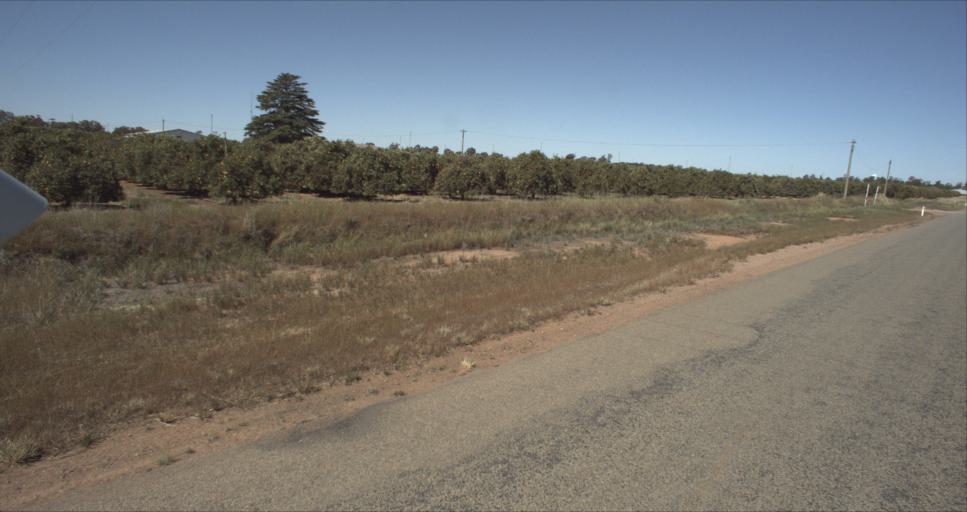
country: AU
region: New South Wales
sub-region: Leeton
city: Leeton
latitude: -34.5416
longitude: 146.3637
